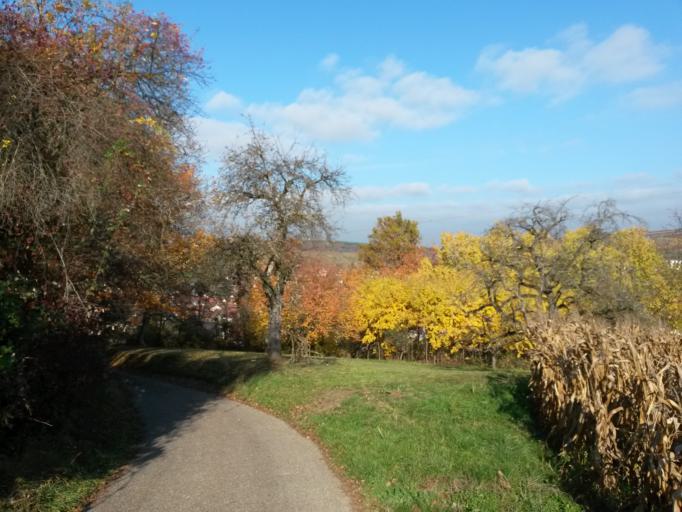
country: DE
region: Baden-Wuerttemberg
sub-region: Karlsruhe Region
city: Neuenburg
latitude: 48.8964
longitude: 8.5724
